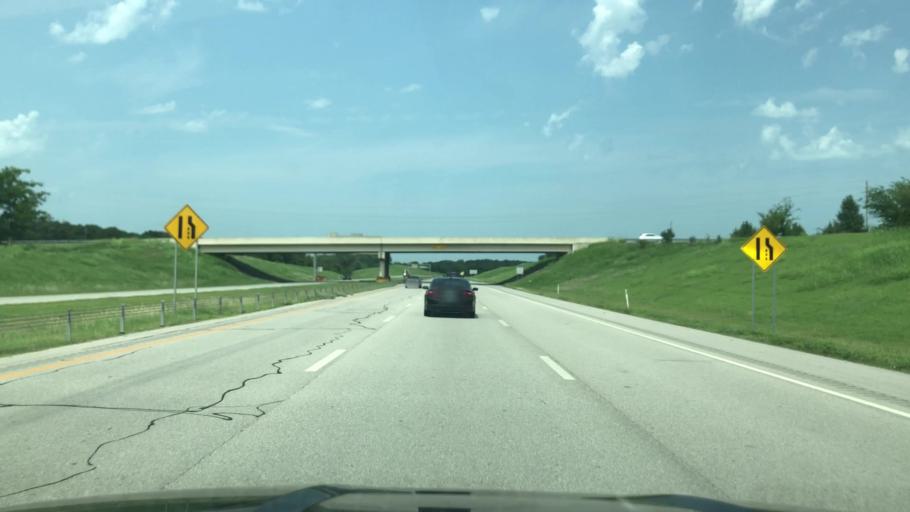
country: US
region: Oklahoma
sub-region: Rogers County
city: Catoosa
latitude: 36.1757
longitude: -95.7319
